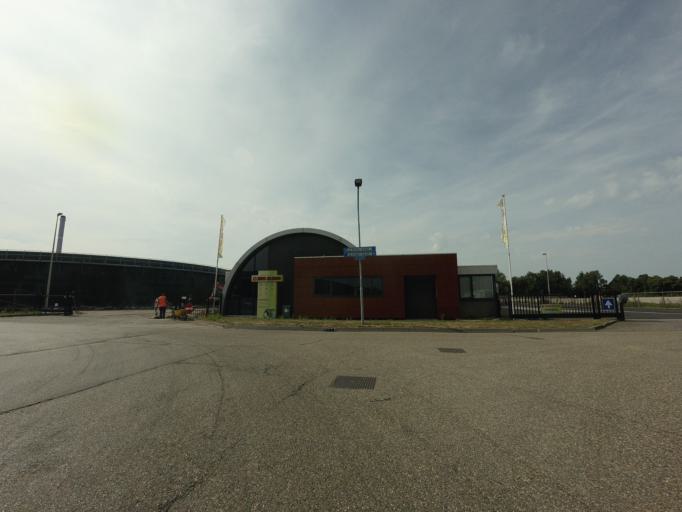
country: NL
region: North Brabant
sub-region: Gemeente Helmond
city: Helmond
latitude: 51.4504
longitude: 5.6970
